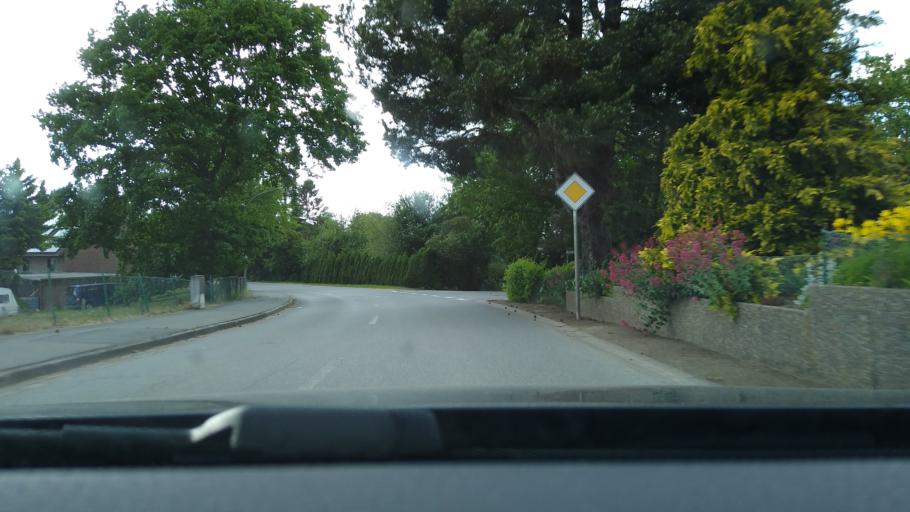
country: DE
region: Schleswig-Holstein
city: Kabelhorst
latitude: 54.2287
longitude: 10.9298
